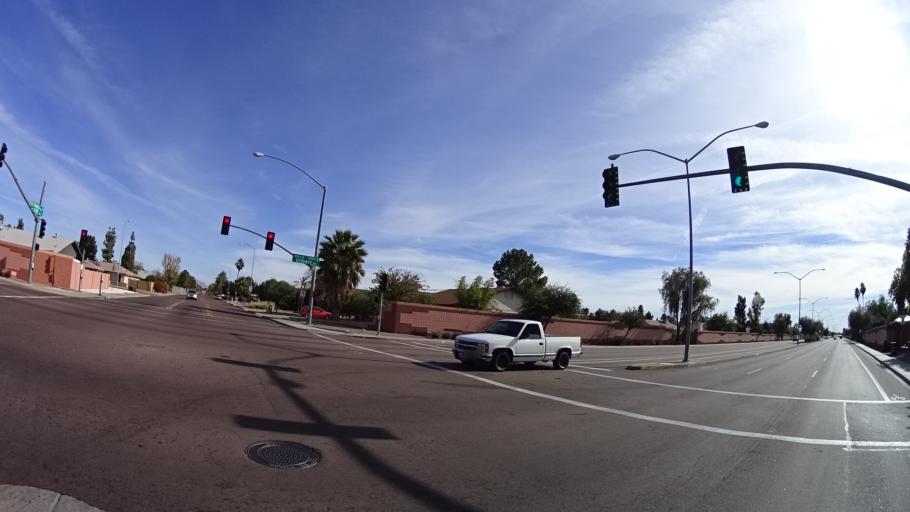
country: US
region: Arizona
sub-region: Maricopa County
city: Mesa
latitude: 33.4009
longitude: -111.7884
